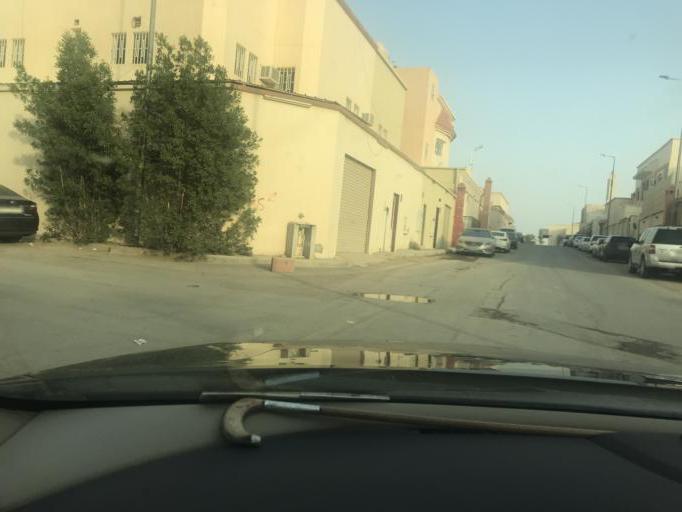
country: SA
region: Ar Riyad
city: Riyadh
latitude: 24.7361
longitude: 46.7768
